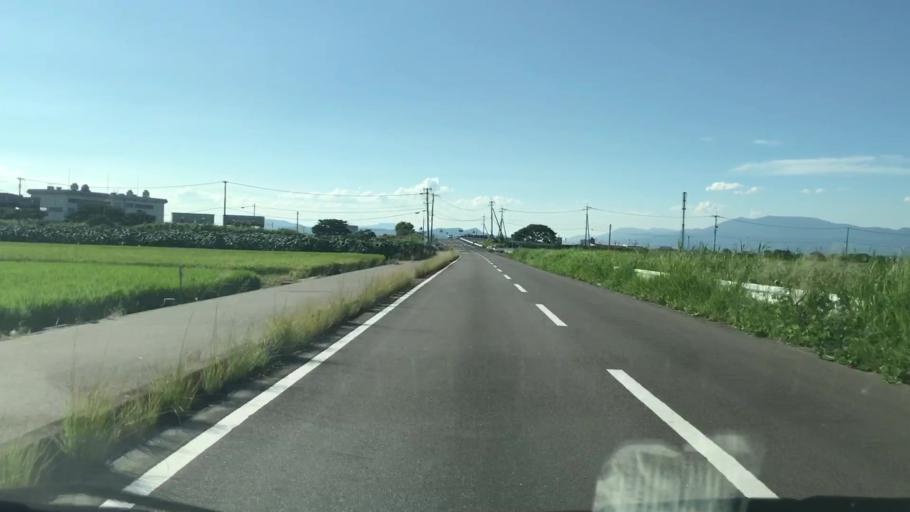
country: JP
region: Saga Prefecture
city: Okawa
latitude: 33.1849
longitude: 130.2939
